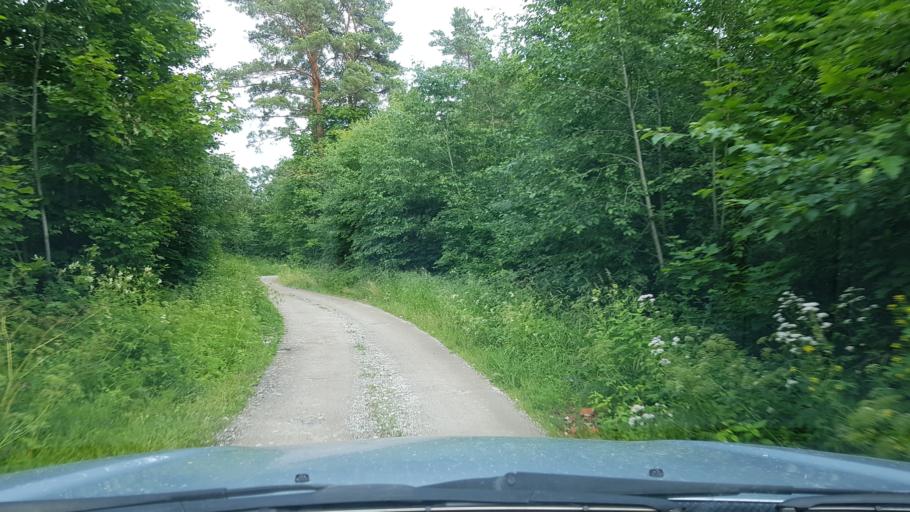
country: EE
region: Ida-Virumaa
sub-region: Narva-Joesuu linn
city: Narva-Joesuu
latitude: 59.4559
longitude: 28.0720
